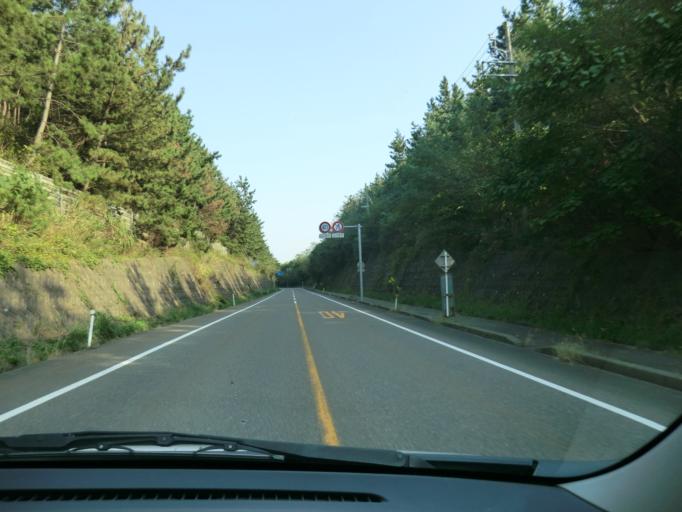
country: JP
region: Niigata
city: Kashiwazaki
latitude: 37.4180
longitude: 138.5906
